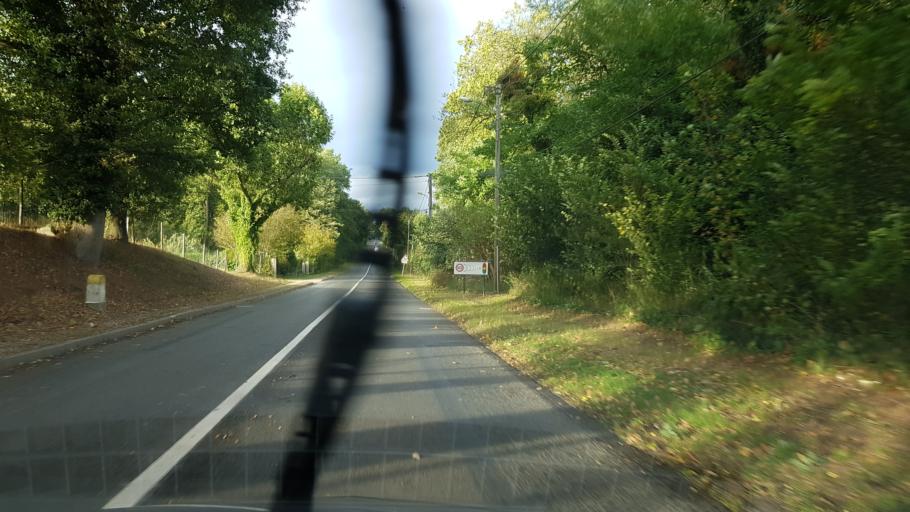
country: FR
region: Ile-de-France
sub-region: Departement de l'Essonne
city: Fontenay-les-Briis
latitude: 48.6145
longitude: 2.1683
